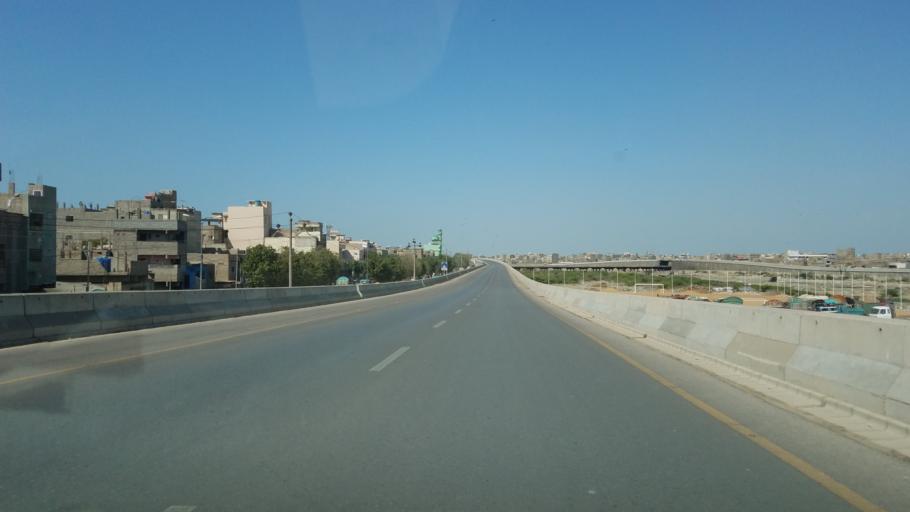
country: PK
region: Sindh
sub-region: Karachi District
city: Karachi
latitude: 24.8805
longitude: 67.0020
